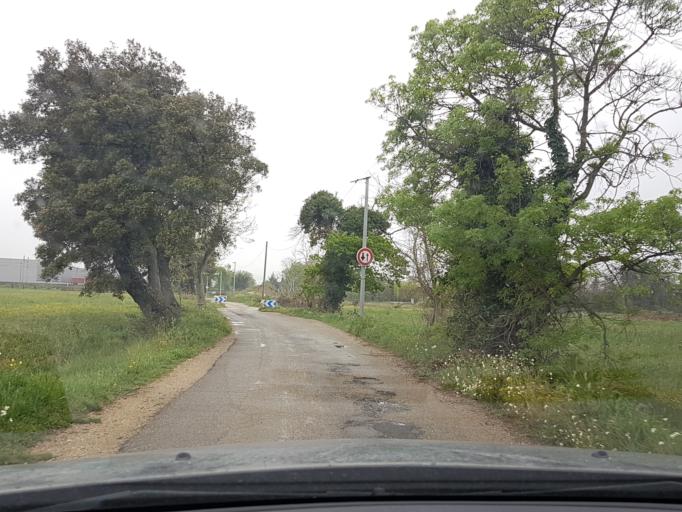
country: FR
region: Provence-Alpes-Cote d'Azur
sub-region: Departement du Vaucluse
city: Sorgues
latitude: 43.9863
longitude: 4.8709
